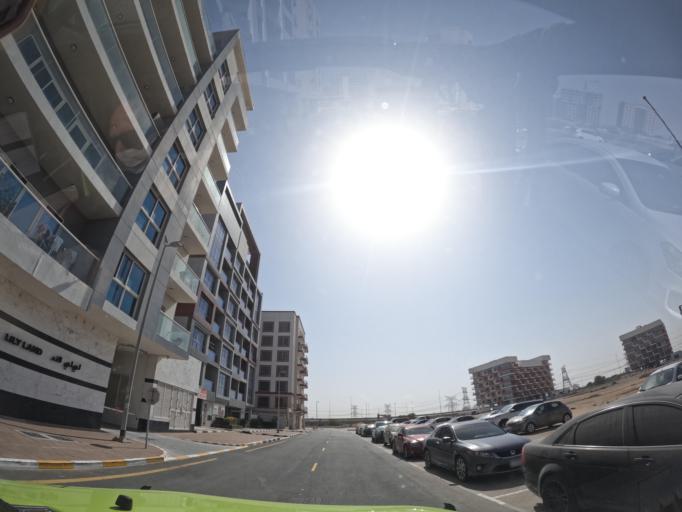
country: AE
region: Dubai
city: Dubai
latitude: 25.0880
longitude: 55.3875
